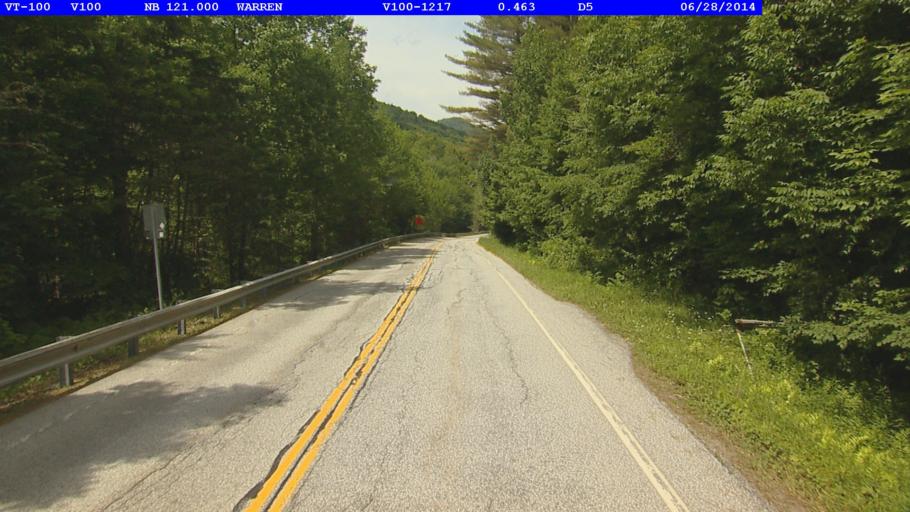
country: US
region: Vermont
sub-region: Washington County
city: Northfield
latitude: 44.0666
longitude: -72.8572
